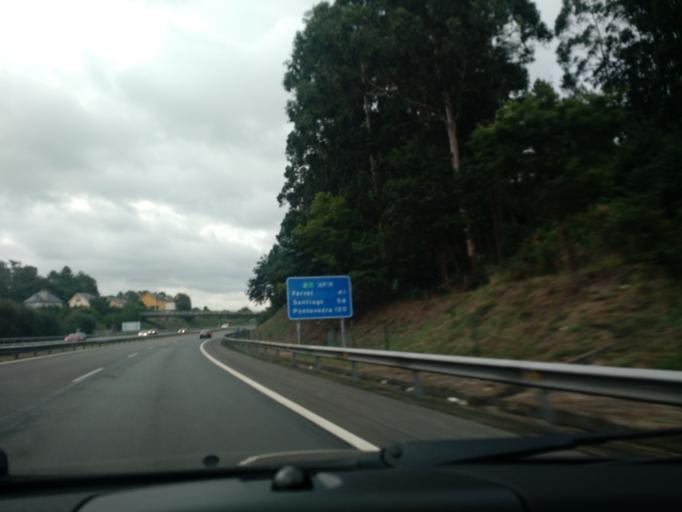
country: ES
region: Galicia
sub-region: Provincia da Coruna
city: Cambre
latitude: 43.3068
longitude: -8.3420
